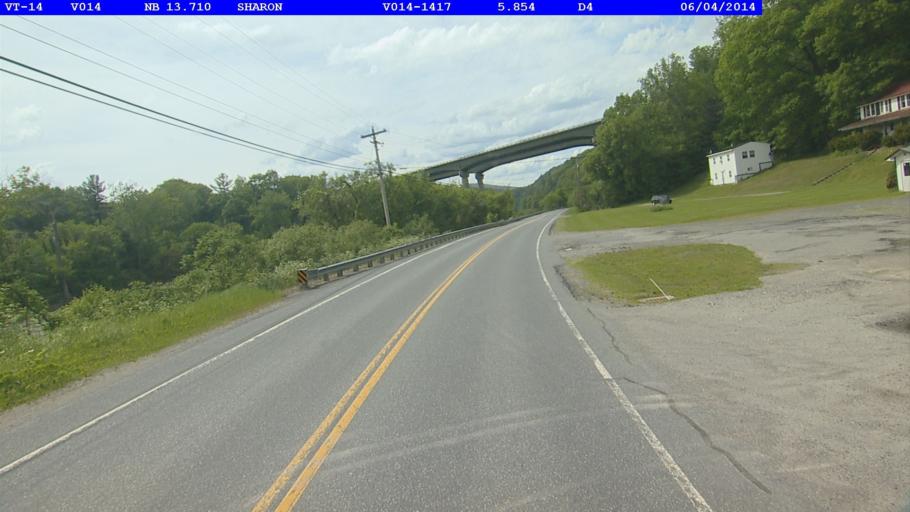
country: US
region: Vermont
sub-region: Windsor County
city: Woodstock
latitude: 43.7810
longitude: -72.4693
